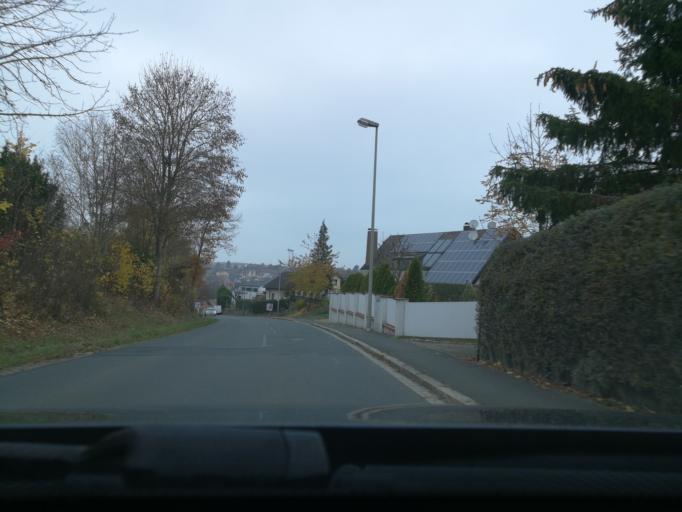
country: DE
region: Bavaria
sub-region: Regierungsbezirk Mittelfranken
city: Puschendorf
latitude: 49.5714
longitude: 10.8286
